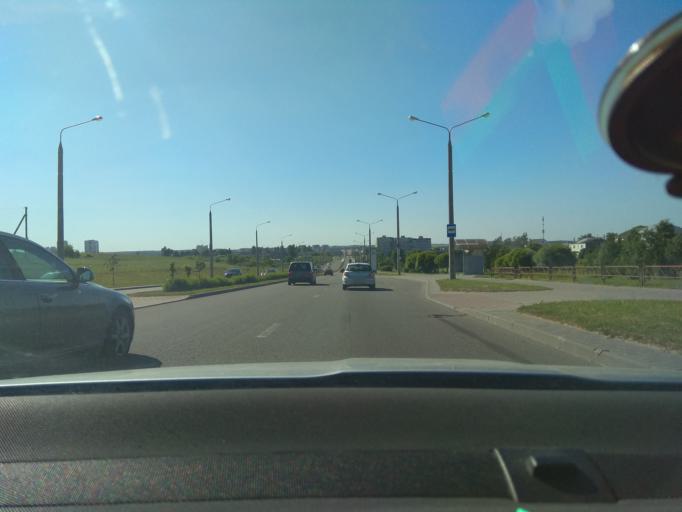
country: BY
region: Grodnenskaya
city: Hrodna
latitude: 53.6477
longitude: 23.8097
